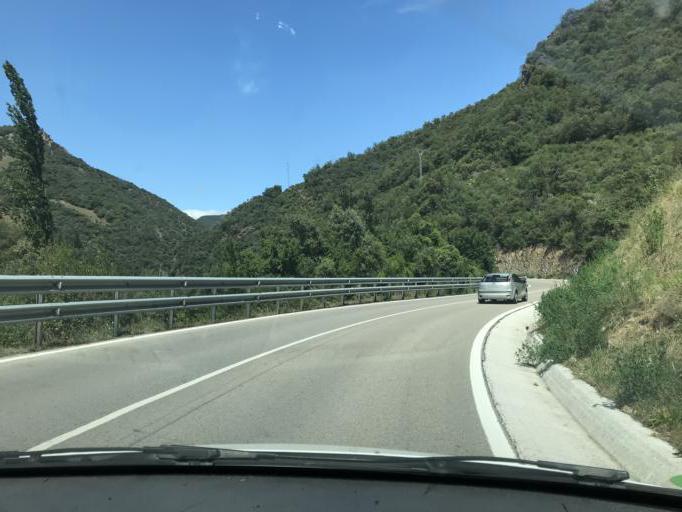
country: ES
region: Cantabria
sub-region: Provincia de Cantabria
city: Cabezon de Liebana
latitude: 43.1074
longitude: -4.5734
